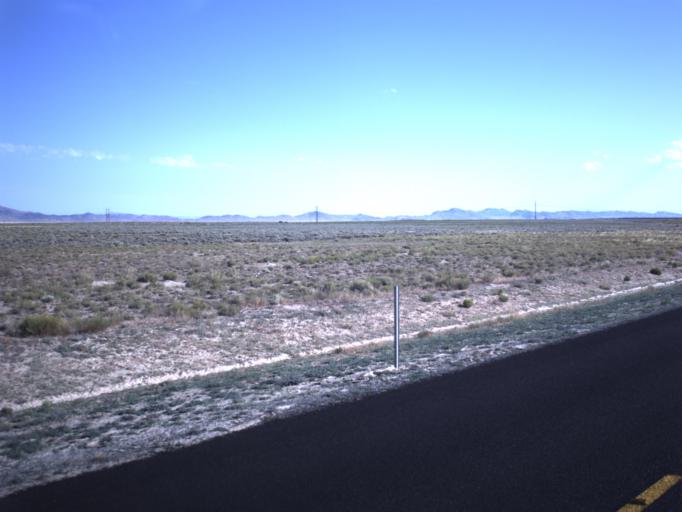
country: US
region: Utah
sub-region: Beaver County
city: Milford
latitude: 38.4749
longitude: -112.9921
